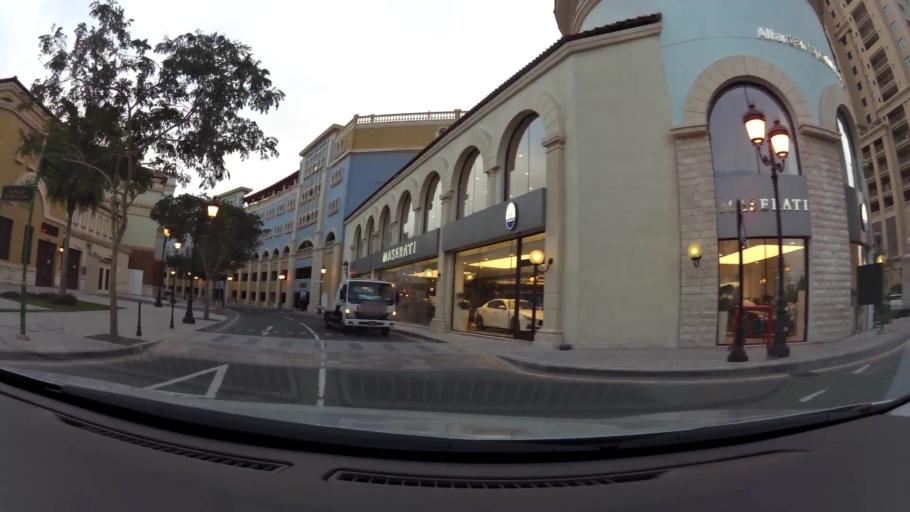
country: QA
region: Baladiyat ad Dawhah
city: Doha
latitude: 25.3668
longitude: 51.5495
